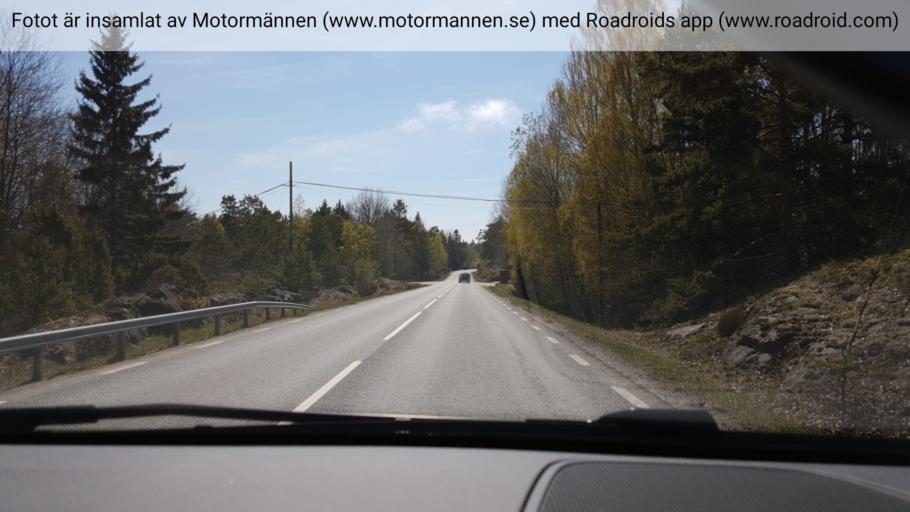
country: SE
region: Stockholm
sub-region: Nynashamns Kommun
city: Nynashamn
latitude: 58.9546
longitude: 18.0154
